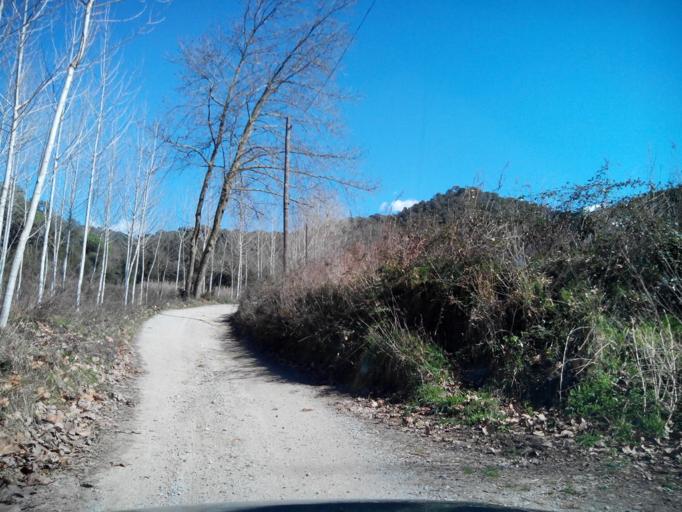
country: ES
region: Catalonia
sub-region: Provincia de Barcelona
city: Sant Andreu de Llavaneres
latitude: 41.6090
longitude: 2.4694
